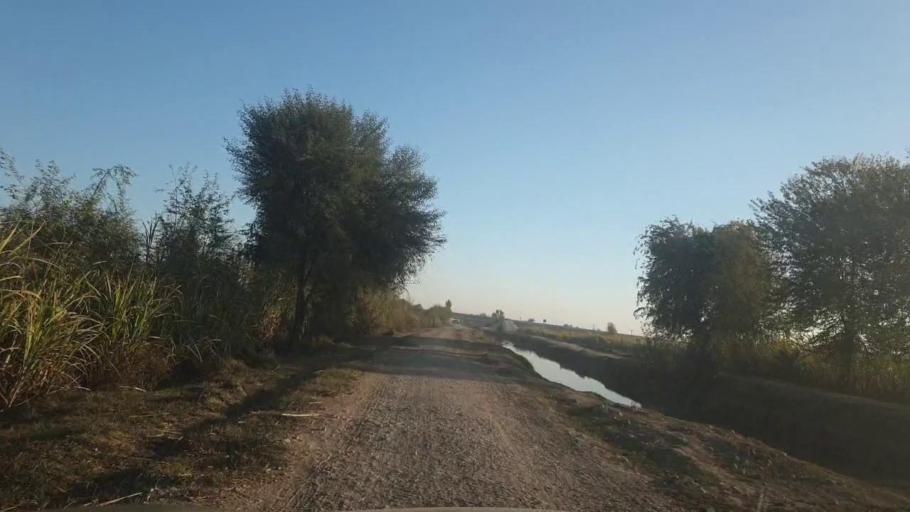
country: PK
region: Sindh
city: Ghotki
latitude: 28.0117
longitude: 69.2686
